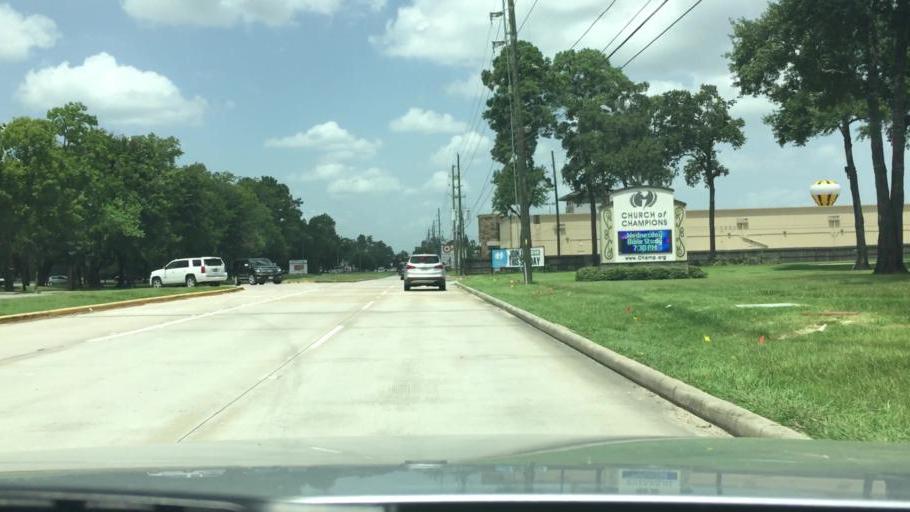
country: US
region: Texas
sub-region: Harris County
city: Hudson
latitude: 29.9655
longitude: -95.5314
